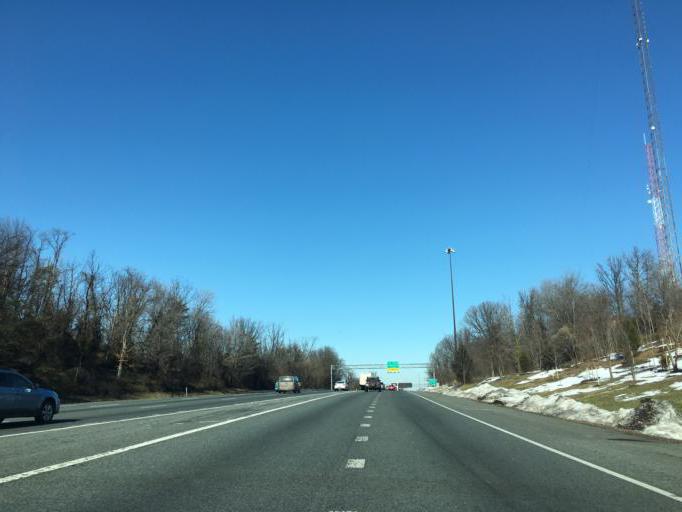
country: US
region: Maryland
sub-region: Baltimore County
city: Lansdowne
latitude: 39.2542
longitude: -76.6764
